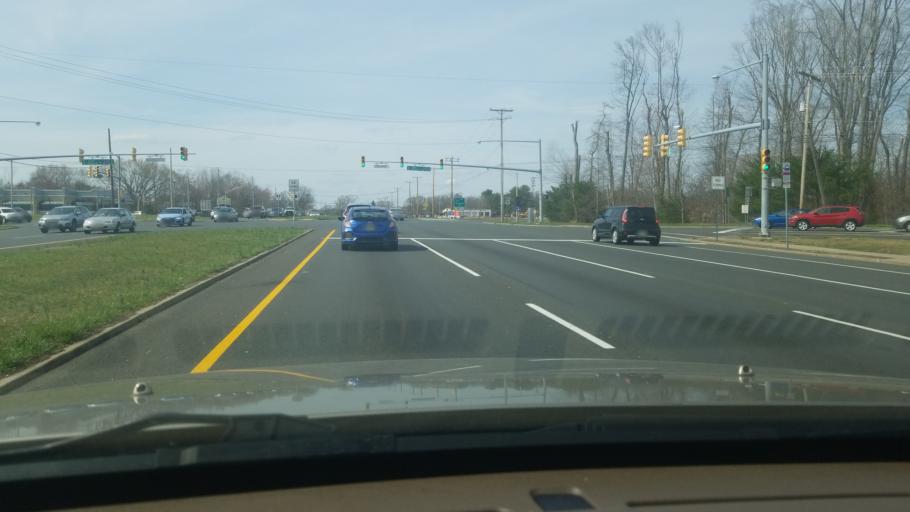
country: US
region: New Jersey
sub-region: Monmouth County
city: Freehold
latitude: 40.2209
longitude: -74.2666
